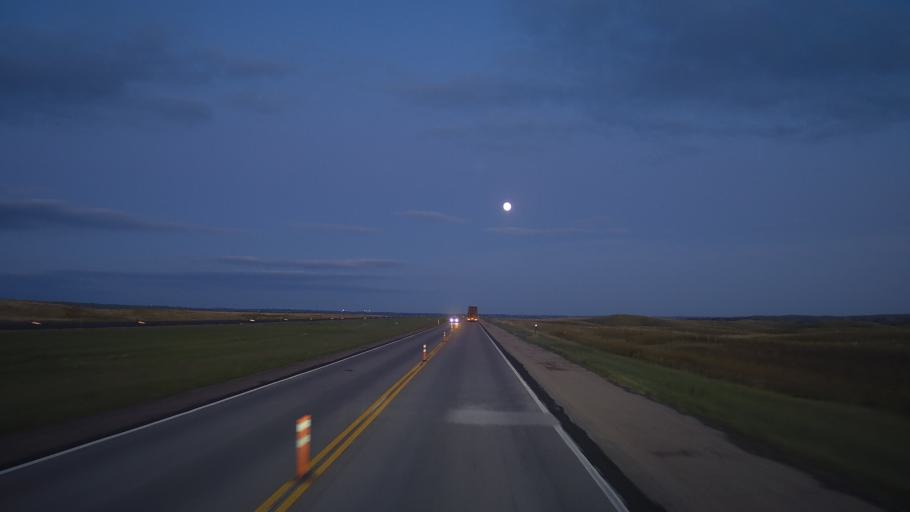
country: US
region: South Dakota
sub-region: Brule County
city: Chamberlain
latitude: 43.8397
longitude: -99.4798
